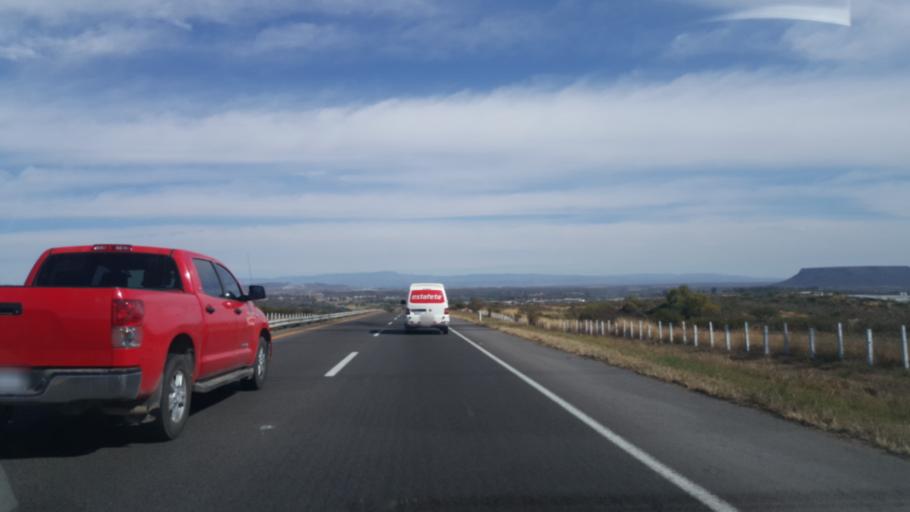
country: MX
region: Jalisco
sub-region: Lagos de Moreno
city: Cristeros [Fraccionamiento]
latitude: 21.3084
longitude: -102.0742
